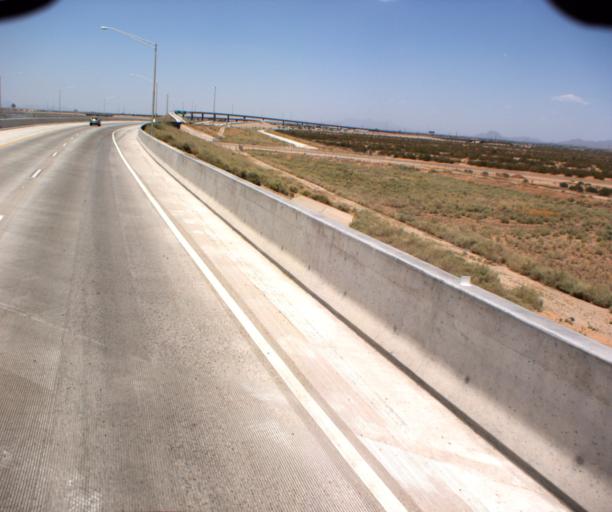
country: US
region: Arizona
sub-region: Maricopa County
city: Queen Creek
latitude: 33.3210
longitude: -111.6419
